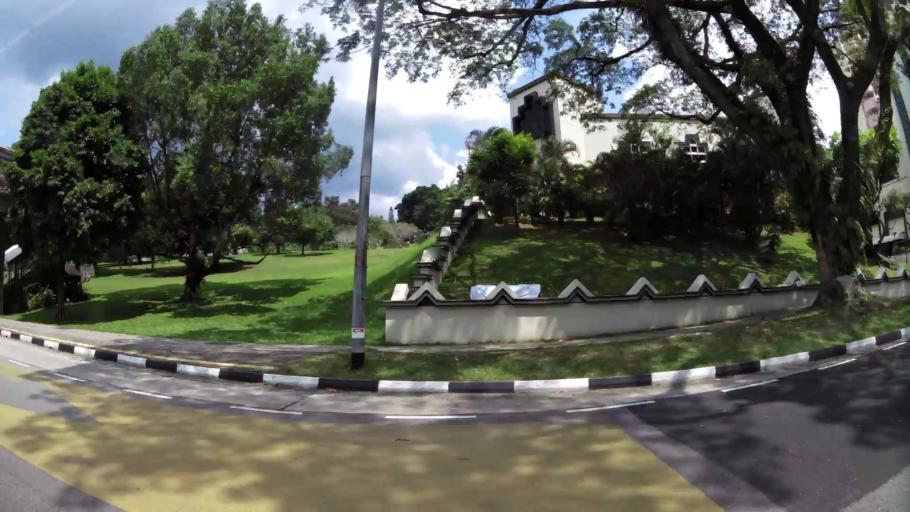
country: MY
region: Johor
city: Kampung Pasir Gudang Baru
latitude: 1.4368
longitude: 103.8339
